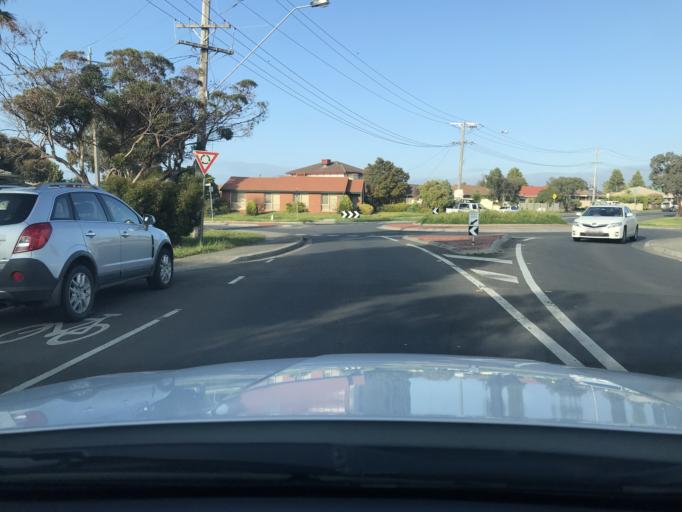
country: AU
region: Victoria
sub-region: Hume
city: Craigieburn
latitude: -37.6108
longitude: 144.9356
